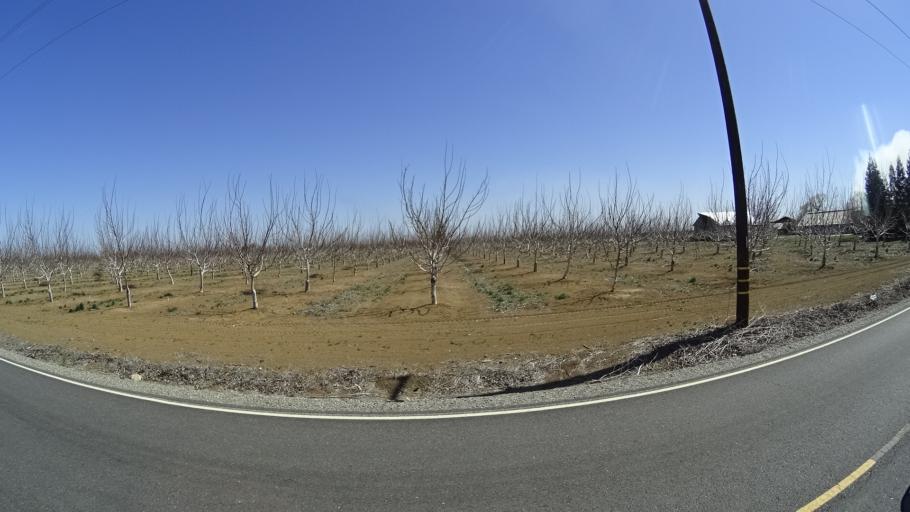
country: US
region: California
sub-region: Glenn County
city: Willows
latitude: 39.5008
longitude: -122.2491
